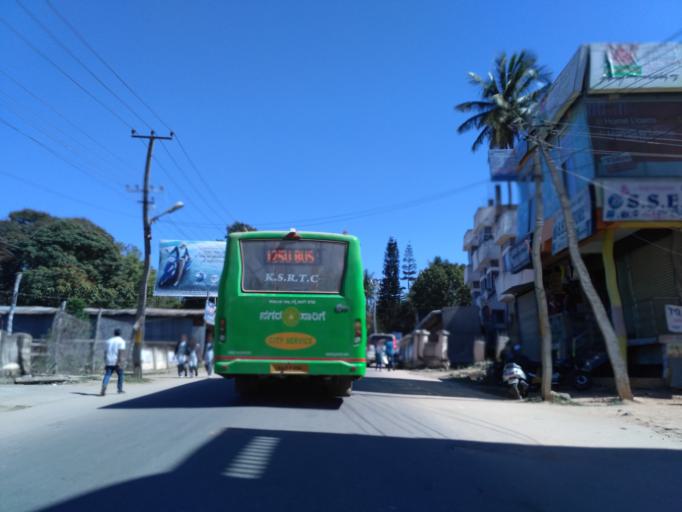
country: IN
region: Karnataka
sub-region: Hassan
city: Hassan
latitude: 13.0067
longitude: 76.1015
